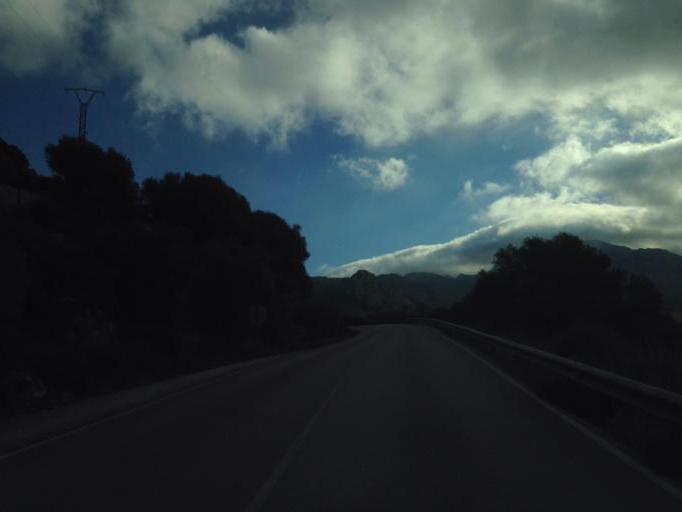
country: ES
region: Andalusia
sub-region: Provincia de Malaga
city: Casabermeja
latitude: 36.9562
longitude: -4.4340
